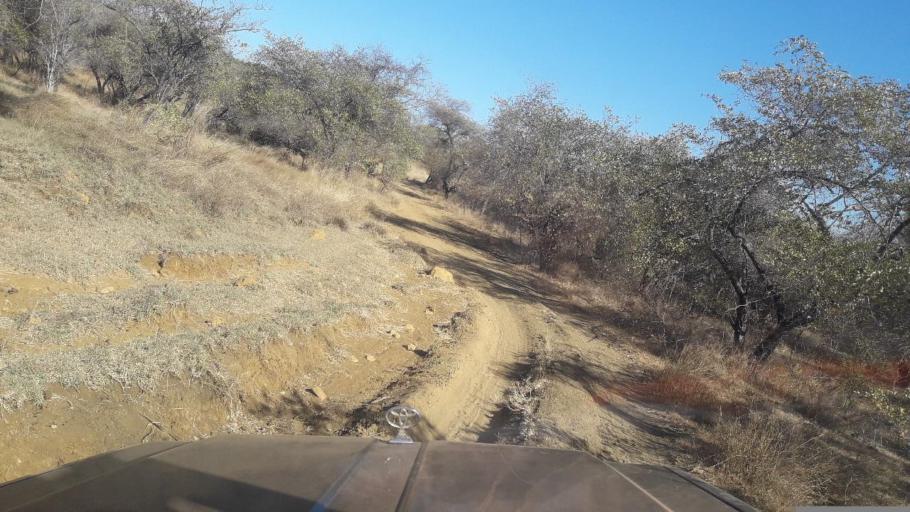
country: MG
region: Boeny
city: Sitampiky
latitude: -16.3916
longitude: 45.5926
